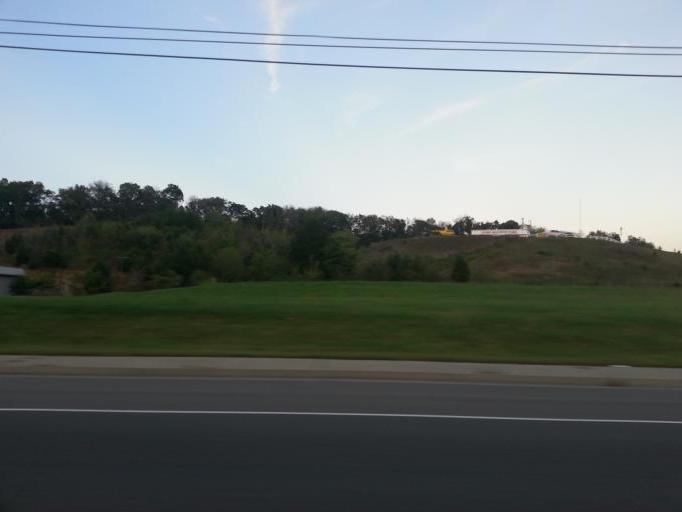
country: US
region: Tennessee
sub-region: Sevier County
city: Sevierville
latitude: 35.9227
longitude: -83.5813
